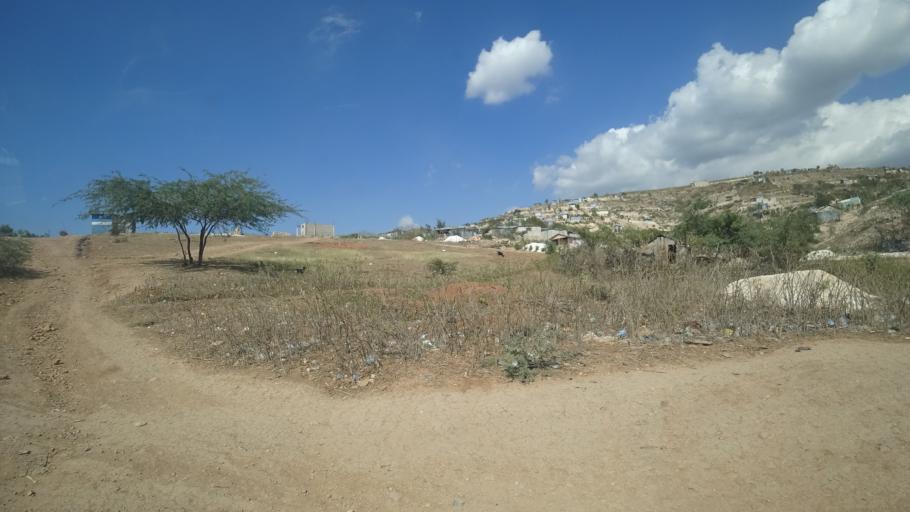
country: HT
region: Ouest
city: Croix des Bouquets
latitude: 18.6734
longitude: -72.2988
